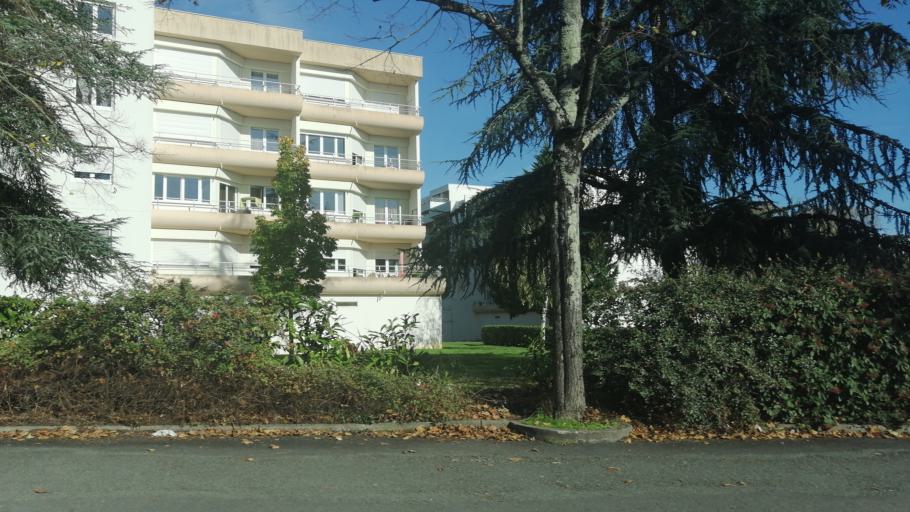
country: FR
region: Poitou-Charentes
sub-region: Departement de la Vienne
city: Poitiers
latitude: 46.5879
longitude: 0.3642
